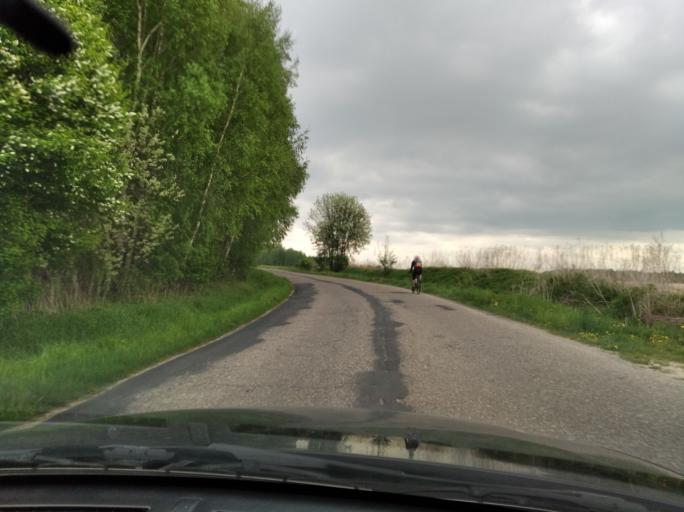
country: PL
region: Lesser Poland Voivodeship
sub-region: Powiat tarnowski
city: Szynwald
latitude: 49.9840
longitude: 21.1327
